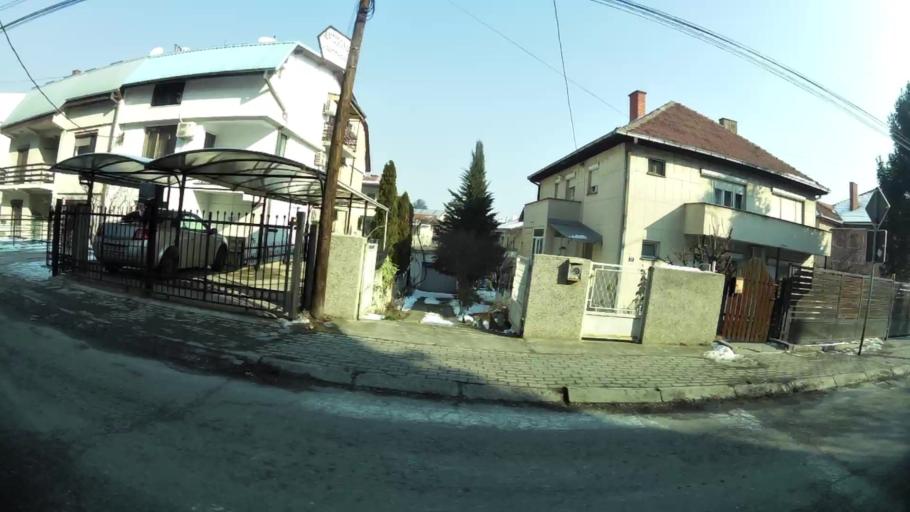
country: MK
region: Karpos
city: Skopje
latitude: 41.9791
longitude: 21.4332
